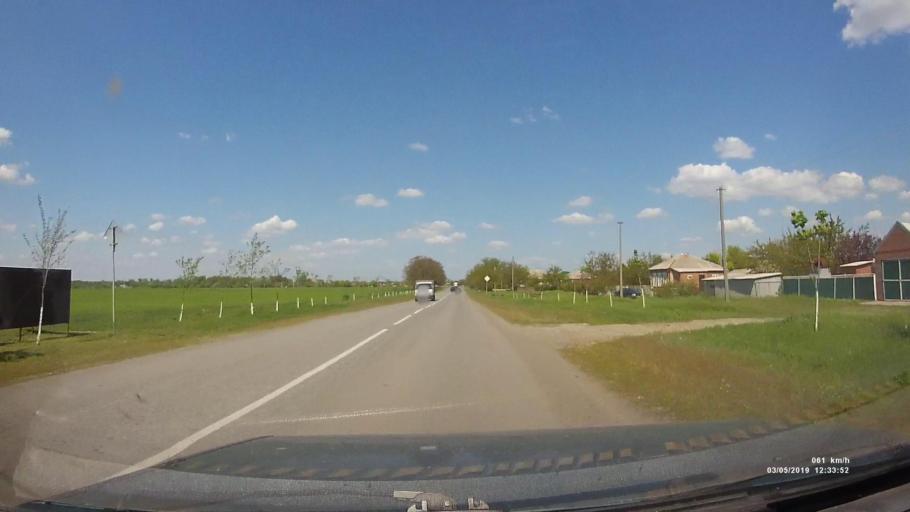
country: RU
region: Rostov
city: Semikarakorsk
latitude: 47.5164
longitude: 40.7710
